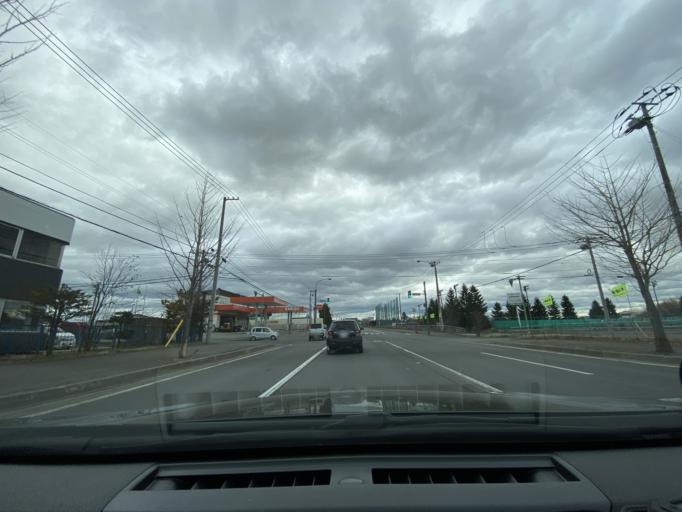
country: JP
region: Hokkaido
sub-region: Asahikawa-shi
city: Asahikawa
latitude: 43.8183
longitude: 142.4069
